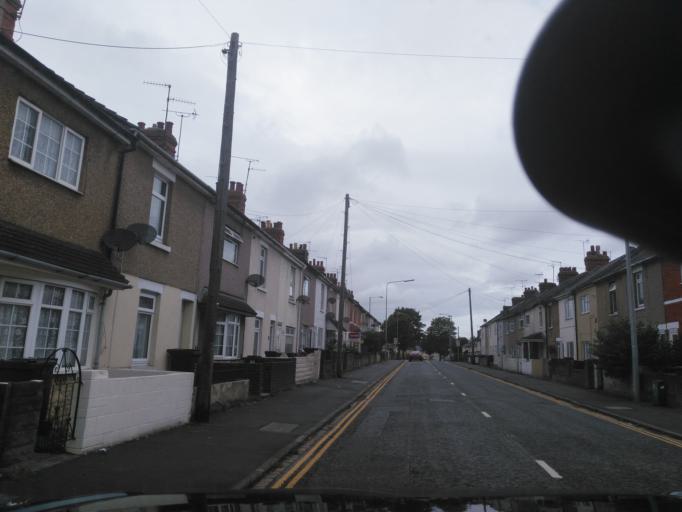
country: GB
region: England
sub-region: Borough of Swindon
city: Swindon
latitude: 51.5723
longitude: -1.7860
